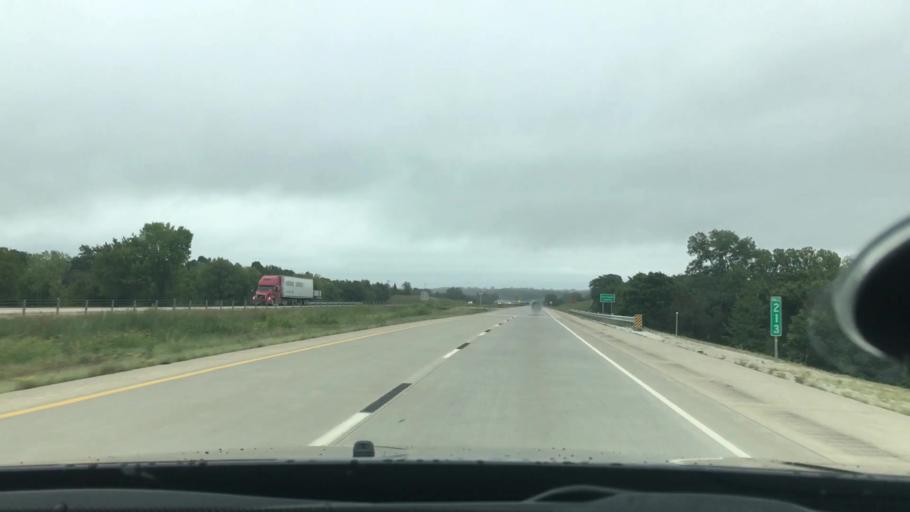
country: US
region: Oklahoma
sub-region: Okfuskee County
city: Boley
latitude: 35.3871
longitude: -96.4430
